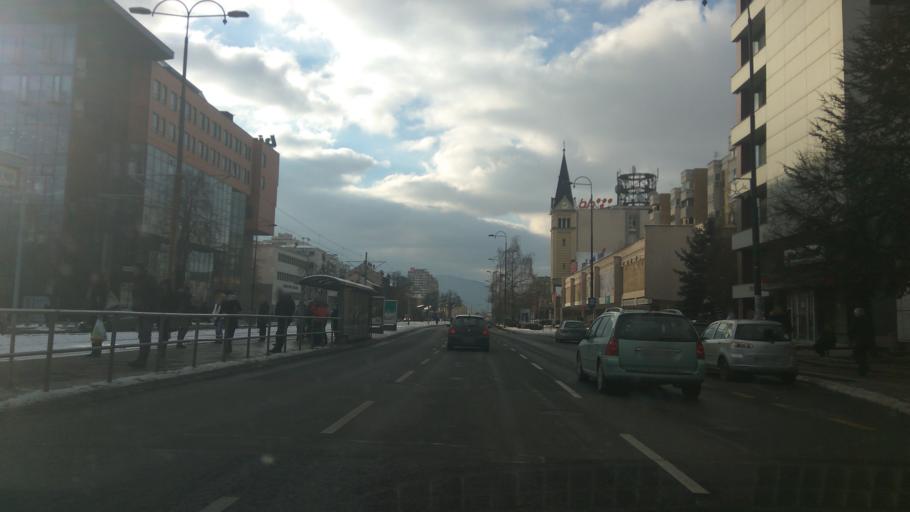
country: BA
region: Federation of Bosnia and Herzegovina
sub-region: Kanton Sarajevo
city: Sarajevo
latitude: 43.8527
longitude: 18.3849
